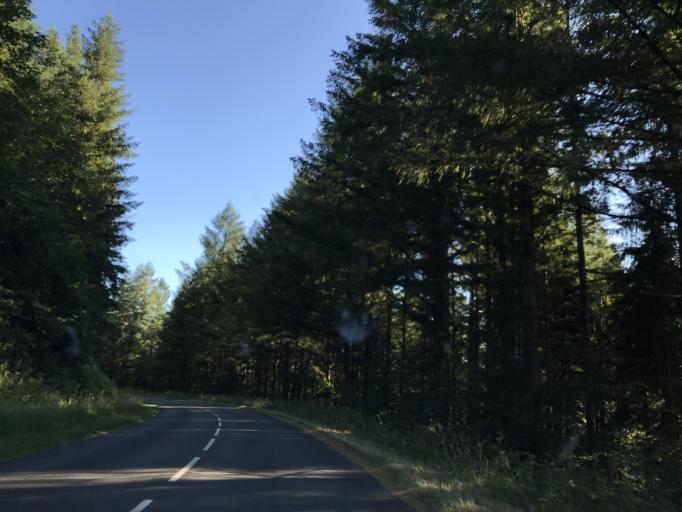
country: FR
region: Auvergne
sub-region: Departement du Puy-de-Dome
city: Celles-sur-Durolle
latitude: 45.8585
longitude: 3.6540
